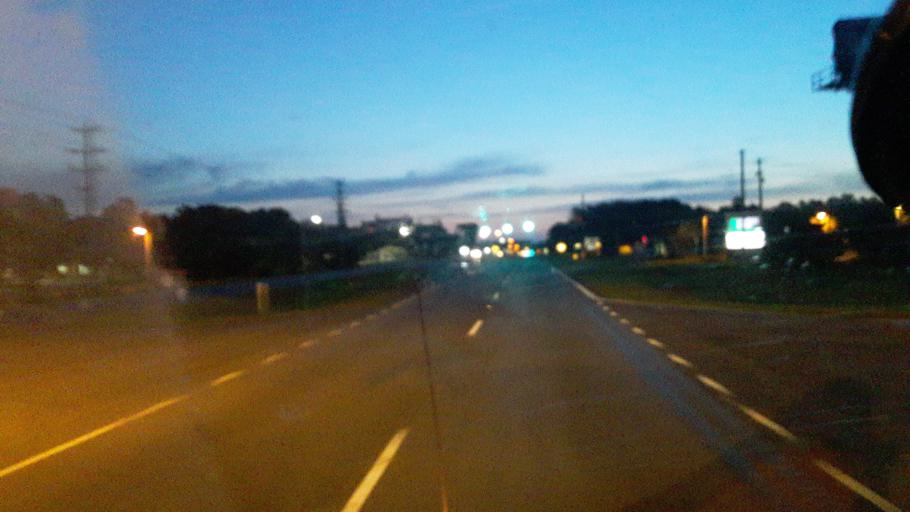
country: US
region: South Carolina
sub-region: Horry County
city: Little River
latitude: 33.8696
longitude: -78.6279
